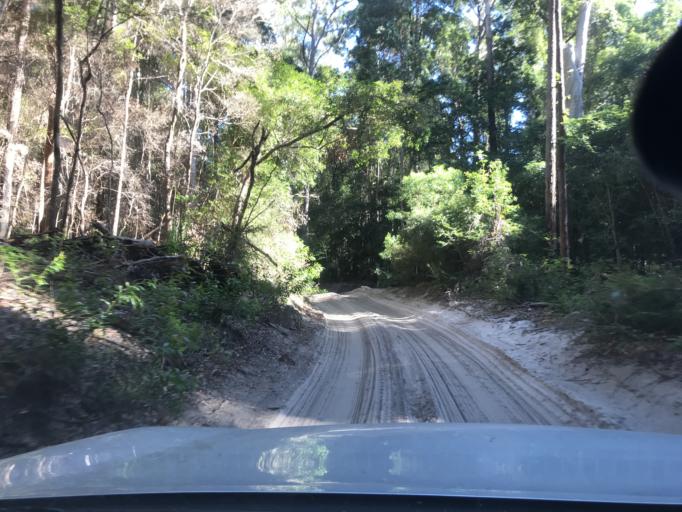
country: AU
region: Queensland
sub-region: Fraser Coast
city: Urangan
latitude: -25.4966
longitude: 153.0950
